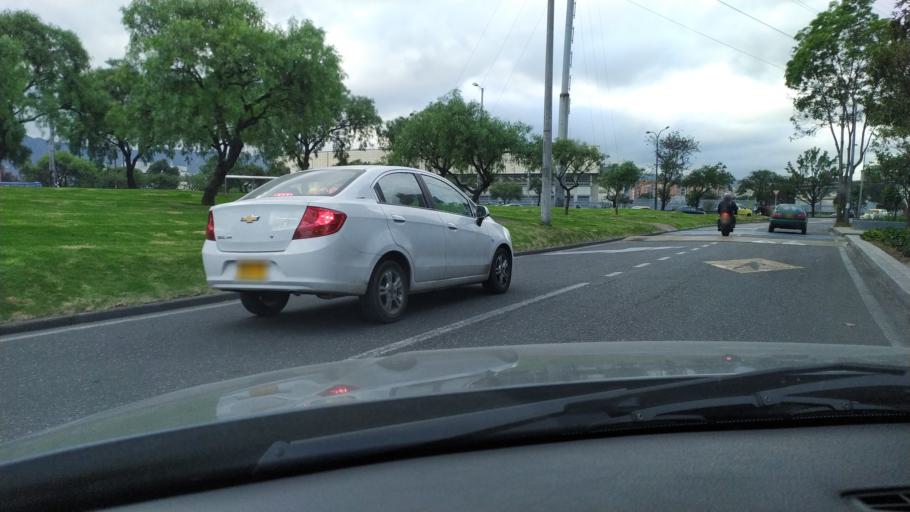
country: CO
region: Bogota D.C.
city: Bogota
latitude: 4.6520
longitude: -74.1055
